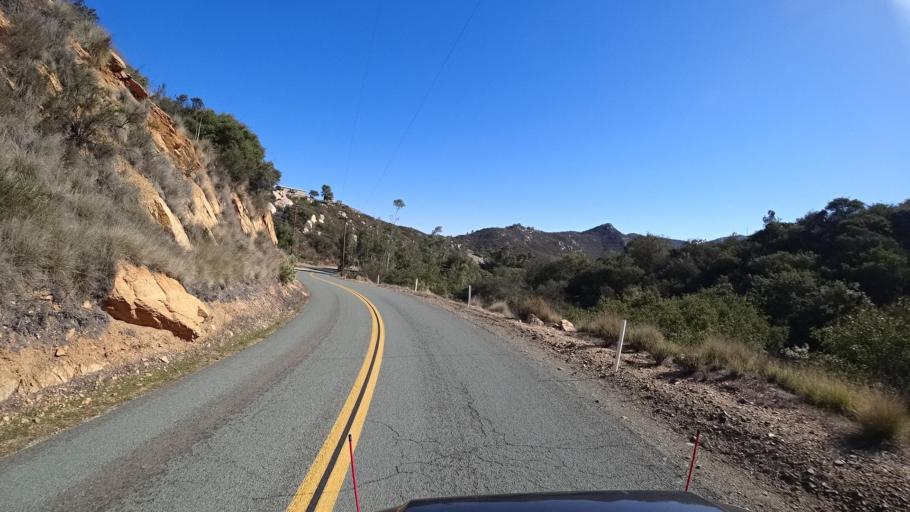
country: US
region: California
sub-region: San Diego County
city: Jamul
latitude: 32.7291
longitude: -116.8234
